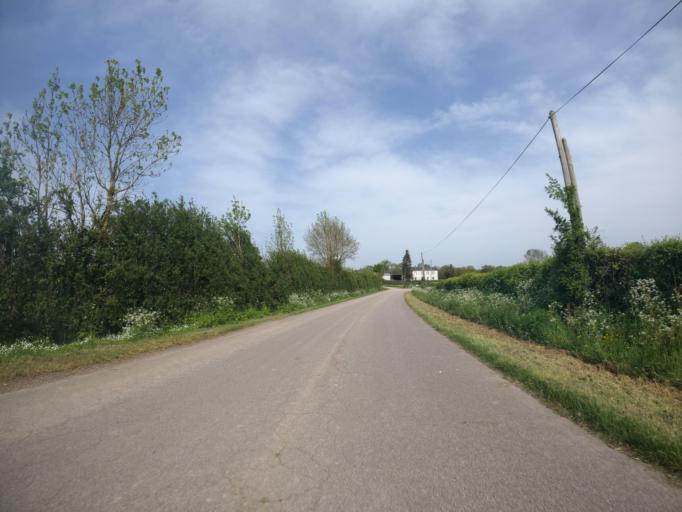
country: FR
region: Poitou-Charentes
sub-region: Departement des Deux-Sevres
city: La Chapelle-Saint-Laurent
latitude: 46.7097
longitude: -0.5086
